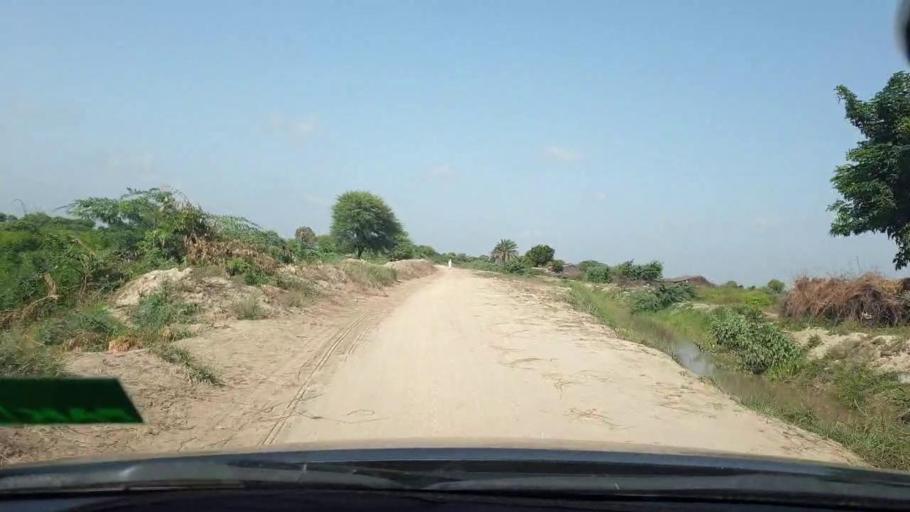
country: PK
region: Sindh
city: Tando Bago
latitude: 24.8757
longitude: 69.0041
